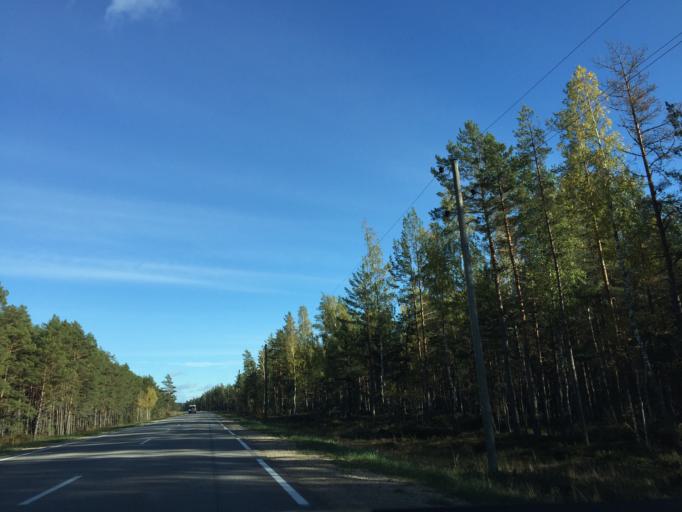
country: LV
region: Engure
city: Smarde
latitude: 57.0347
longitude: 23.4299
